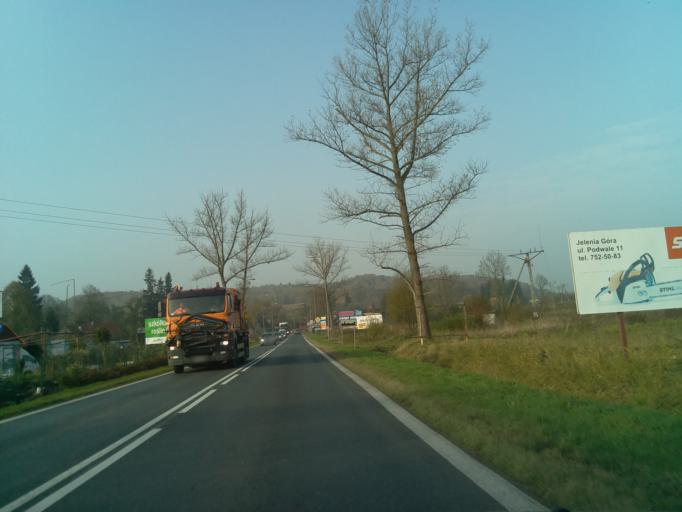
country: PL
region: Lower Silesian Voivodeship
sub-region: Powiat jeleniogorski
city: Janowice Wielkie
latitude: 50.9070
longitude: 15.8451
